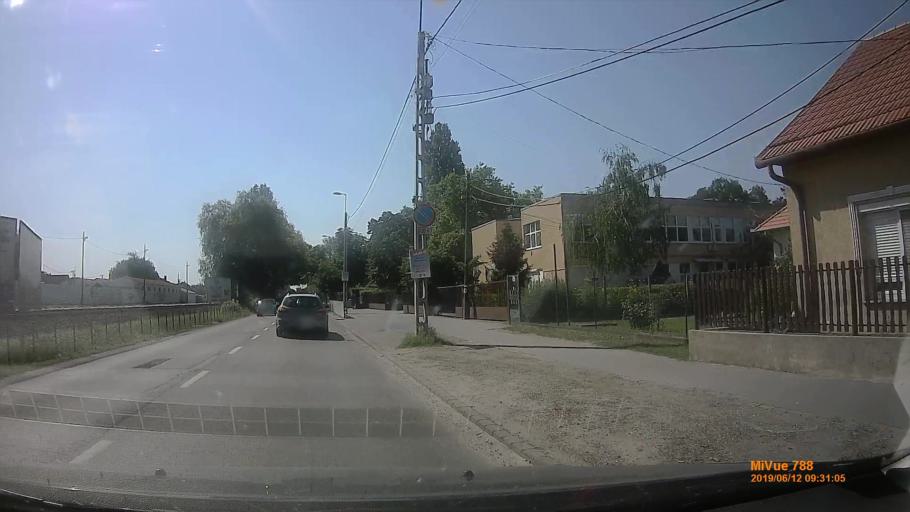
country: HU
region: Pest
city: Gyal
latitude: 47.4028
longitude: 19.1875
